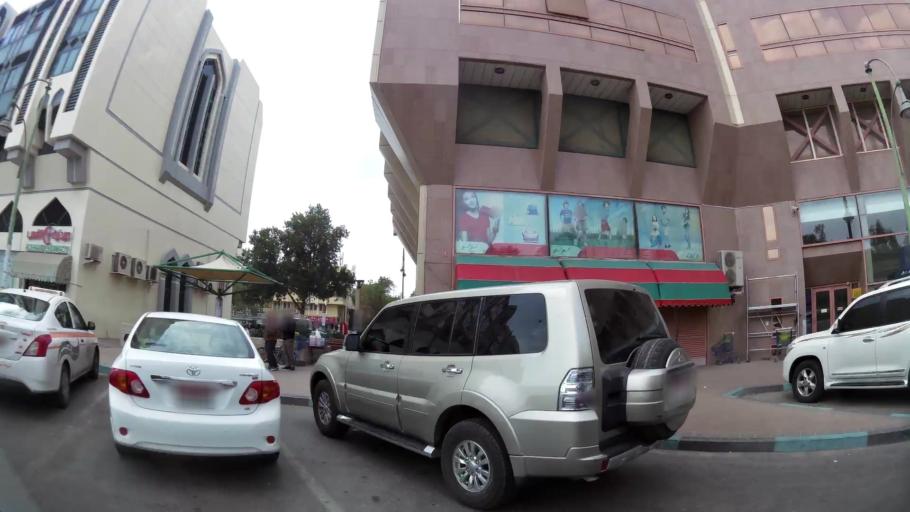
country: AE
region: Abu Dhabi
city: Al Ain
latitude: 24.2191
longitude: 55.7759
